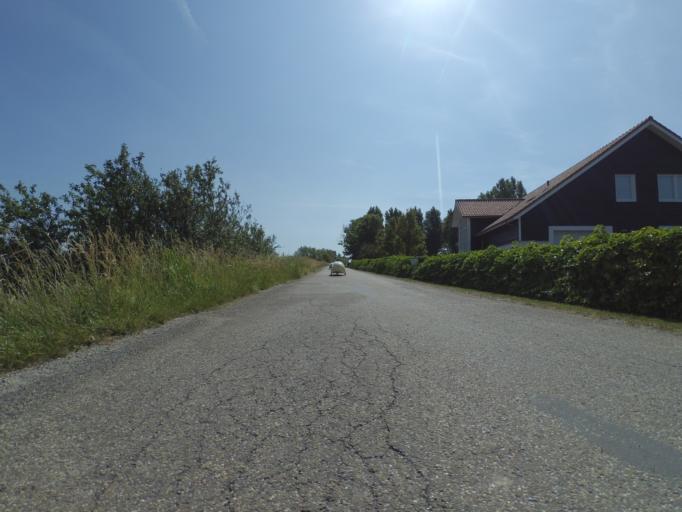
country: NL
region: South Holland
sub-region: Gemeente Goeree-Overflakkee
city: Dirksland
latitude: 51.7065
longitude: 4.1308
